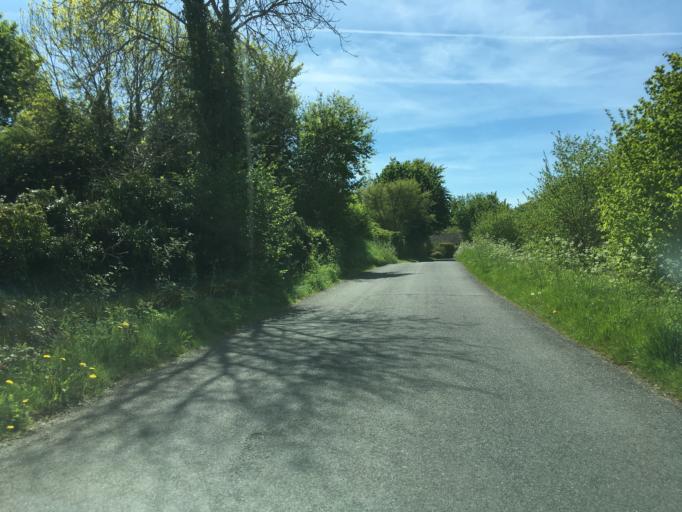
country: GB
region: England
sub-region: Gloucestershire
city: Coates
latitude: 51.7270
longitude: -2.0823
